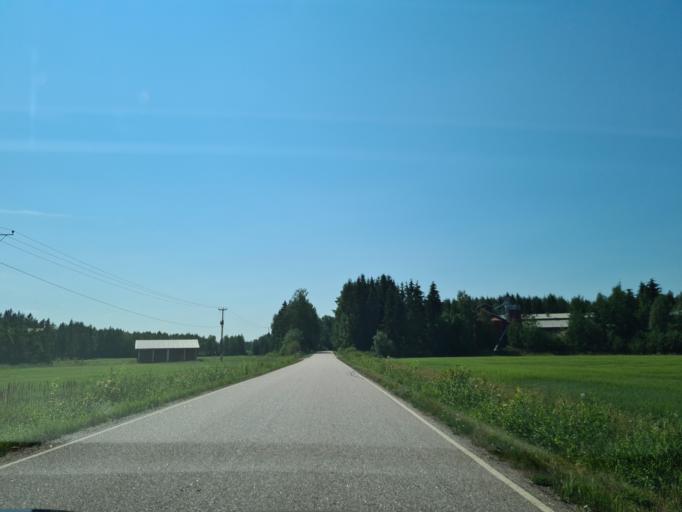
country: FI
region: Varsinais-Suomi
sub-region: Loimaa
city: Aura
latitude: 60.6048
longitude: 22.6081
